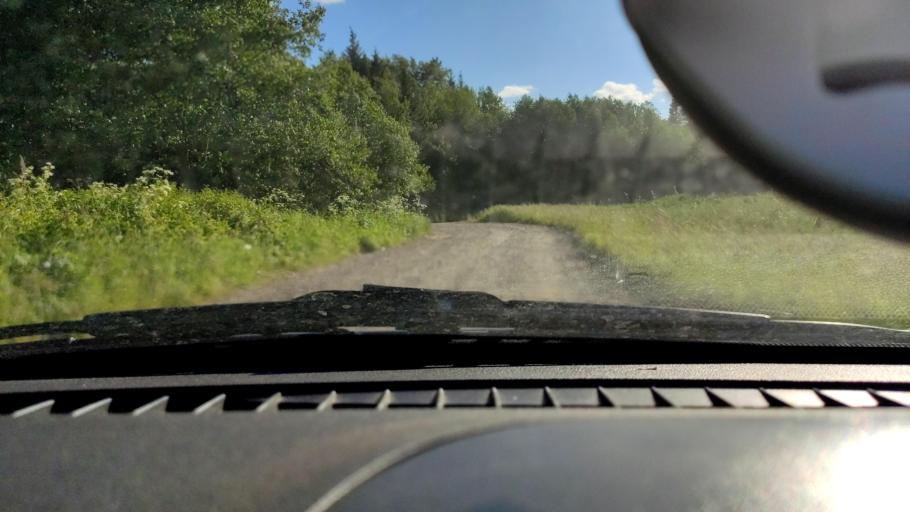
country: RU
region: Perm
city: Bershet'
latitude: 57.6952
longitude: 56.4028
